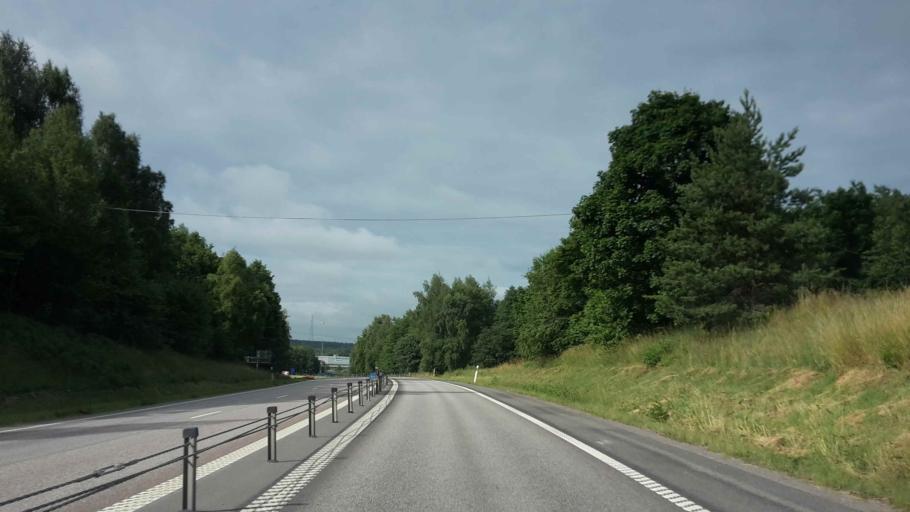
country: SE
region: OEstergoetland
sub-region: Motala Kommun
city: Motala
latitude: 58.5686
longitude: 15.0676
